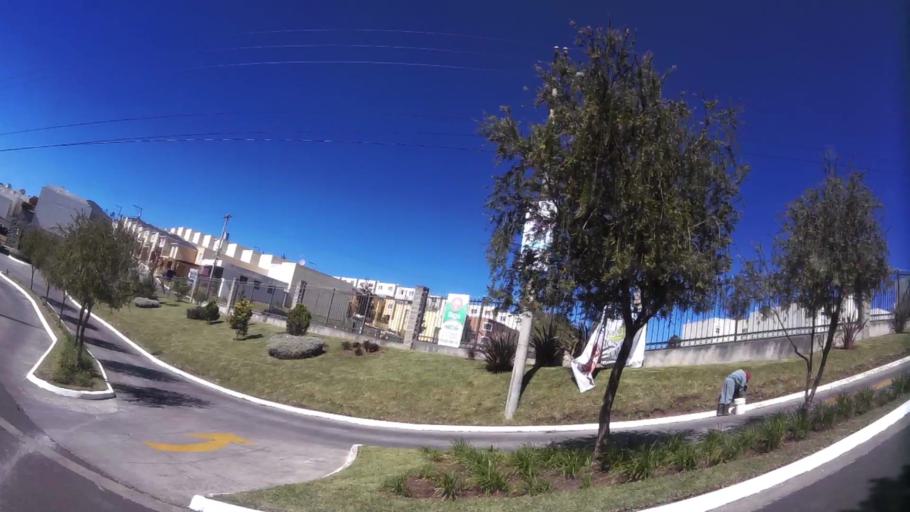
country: GT
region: Guatemala
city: San Jose Pinula
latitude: 14.5187
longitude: -90.4454
